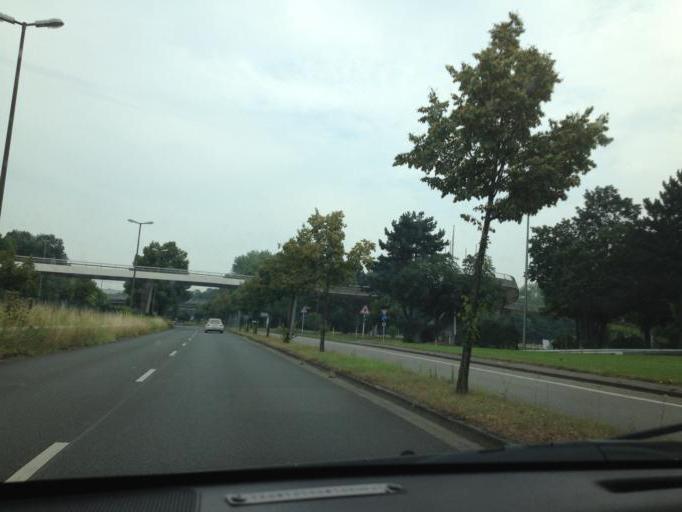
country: DE
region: North Rhine-Westphalia
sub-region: Regierungsbezirk Arnsberg
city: Dortmund
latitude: 51.4924
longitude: 7.4599
